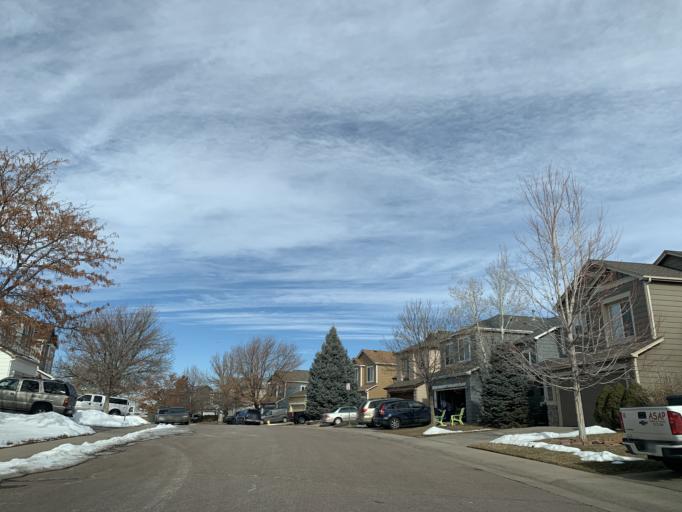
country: US
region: Colorado
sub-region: Douglas County
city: Carriage Club
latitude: 39.5408
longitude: -104.9277
